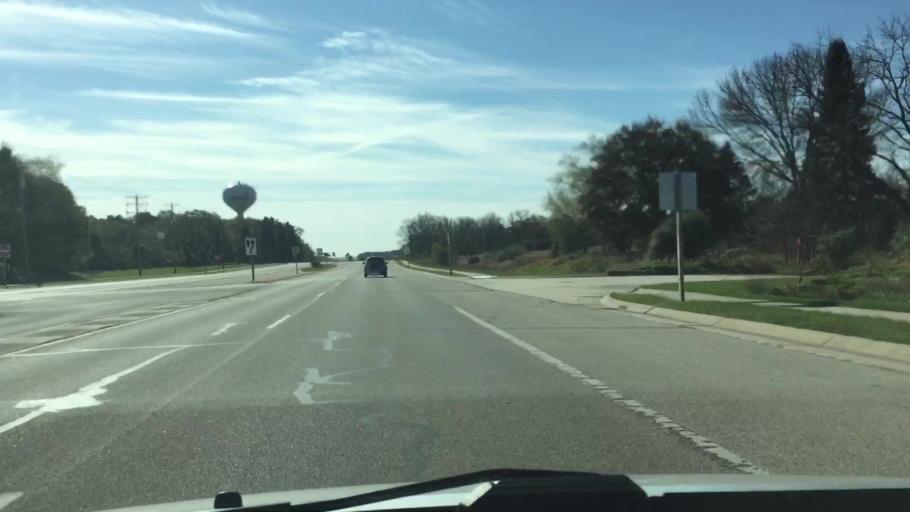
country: US
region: Wisconsin
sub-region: Waukesha County
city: Sussex
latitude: 43.1235
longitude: -88.2444
